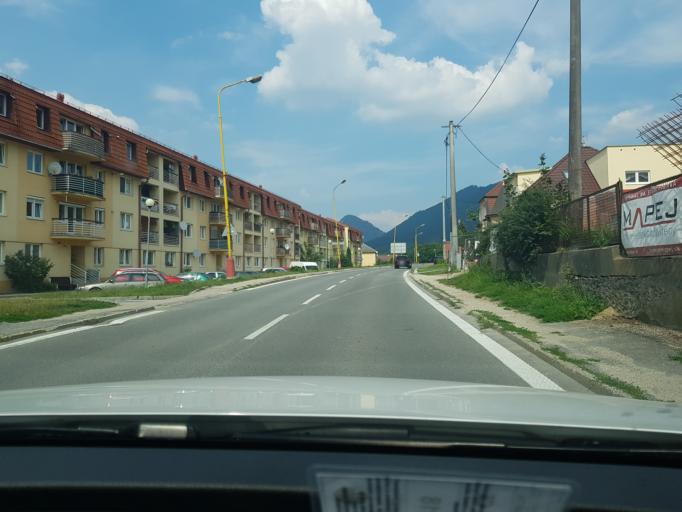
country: SK
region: Trenciansky
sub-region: Okres Povazska Bystrica
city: Povazska Bystrica
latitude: 49.1184
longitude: 18.4531
